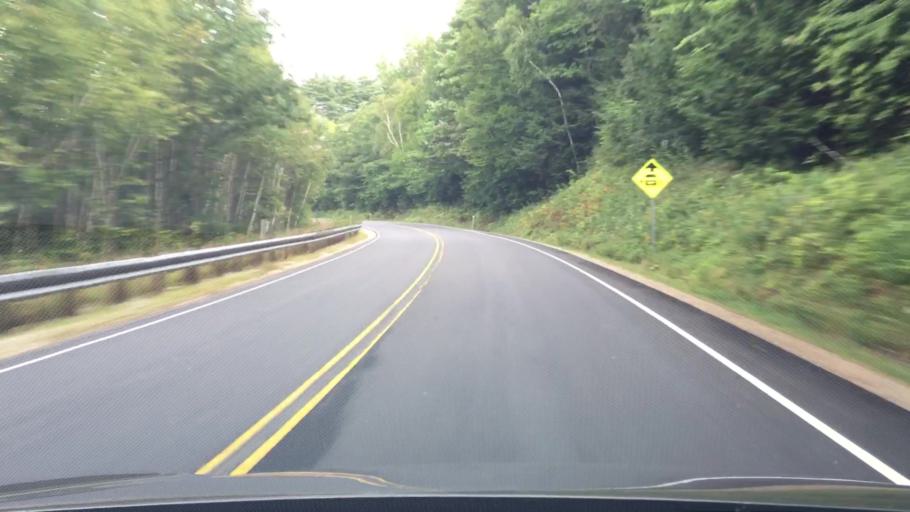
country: US
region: New Hampshire
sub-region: Carroll County
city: Conway
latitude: 43.9892
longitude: -71.1652
